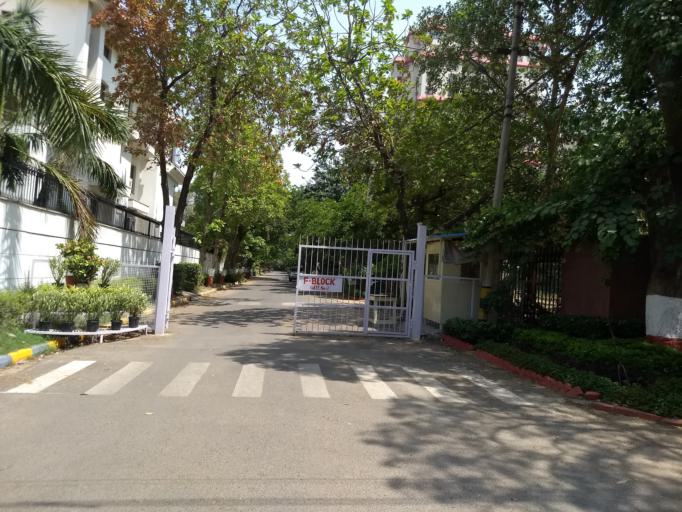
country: IN
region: Haryana
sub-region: Gurgaon
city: Gurgaon
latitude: 28.4582
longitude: 77.0677
